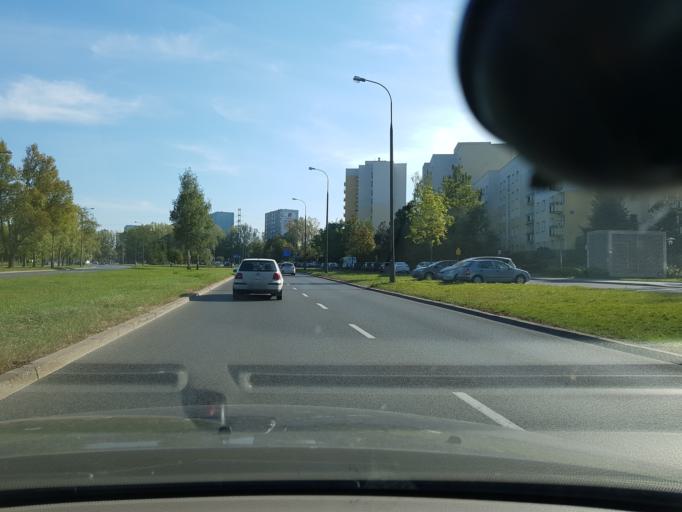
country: PL
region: Masovian Voivodeship
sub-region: Warszawa
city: Ursynow
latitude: 52.1585
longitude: 21.0417
